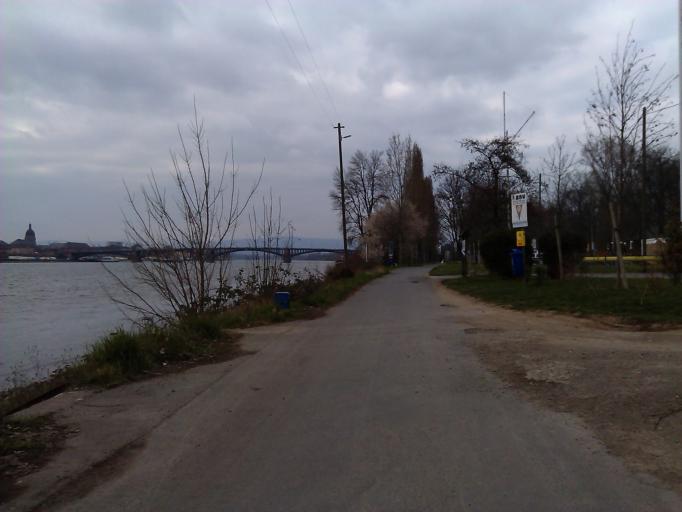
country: DE
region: Rheinland-Pfalz
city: Mainz
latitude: 50.0006
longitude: 8.2862
